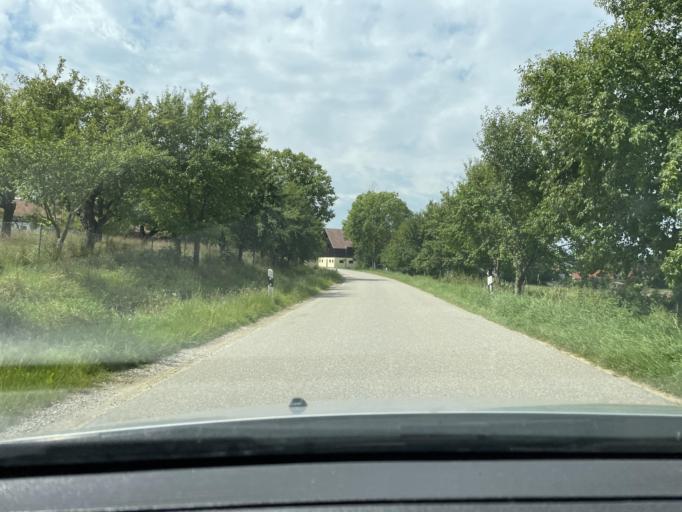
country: DE
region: Bavaria
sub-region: Lower Bavaria
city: Eging
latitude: 48.4470
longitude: 12.2165
